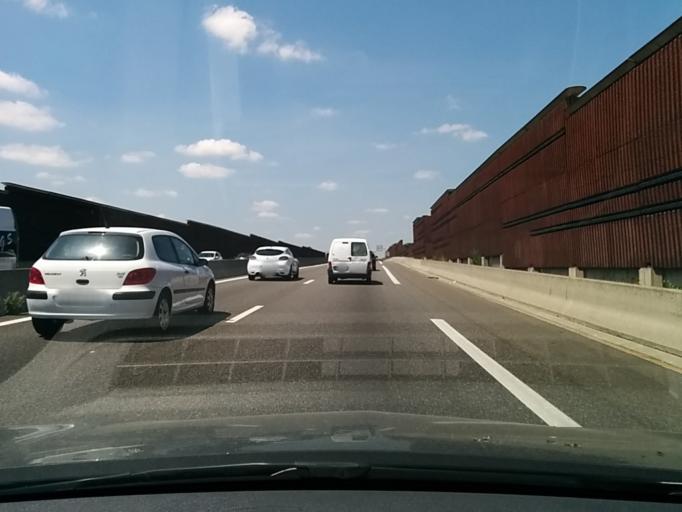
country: FR
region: Midi-Pyrenees
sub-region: Departement de la Haute-Garonne
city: Colomiers
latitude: 43.6052
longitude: 1.3416
